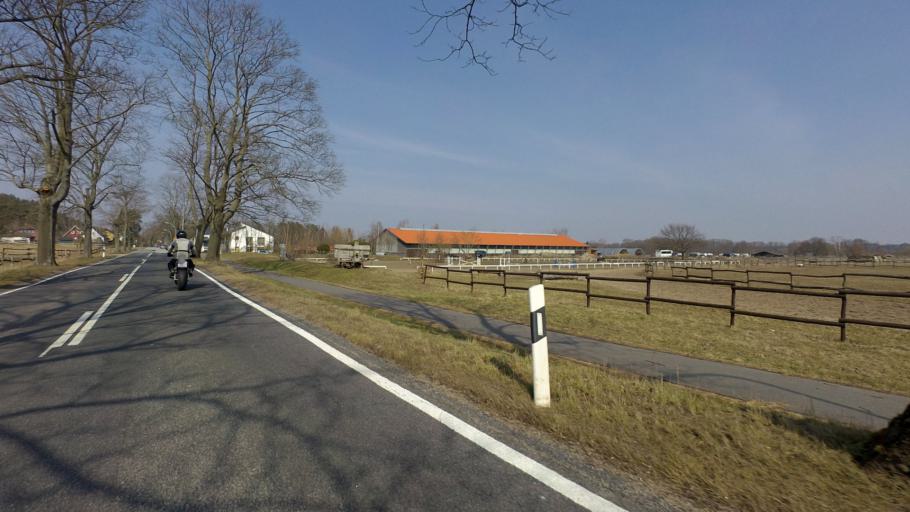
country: DE
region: Brandenburg
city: Werder
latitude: 52.4195
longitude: 12.8942
